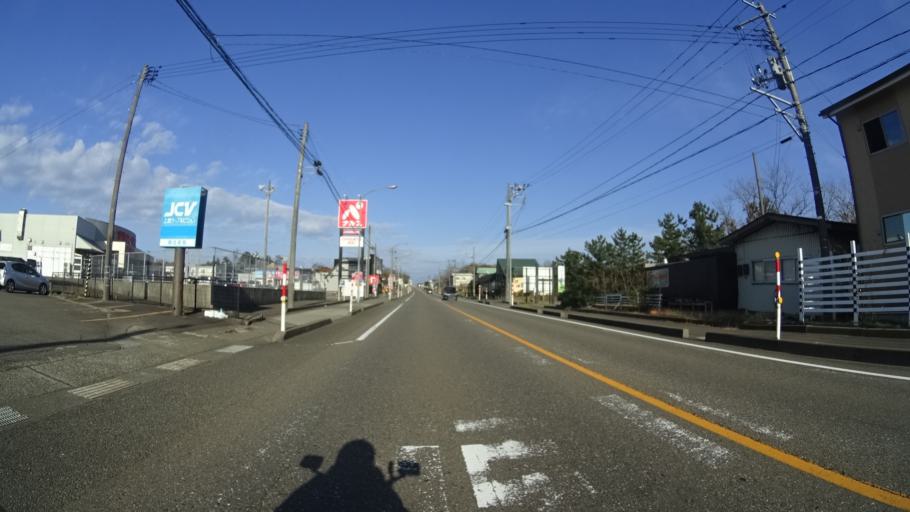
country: JP
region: Niigata
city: Joetsu
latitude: 37.2277
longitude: 138.3312
